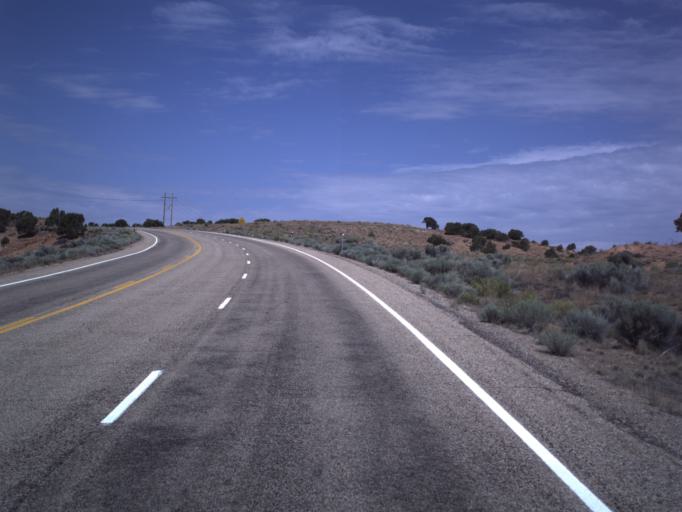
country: US
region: Utah
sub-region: Uintah County
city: Naples
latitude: 40.1407
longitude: -109.2737
